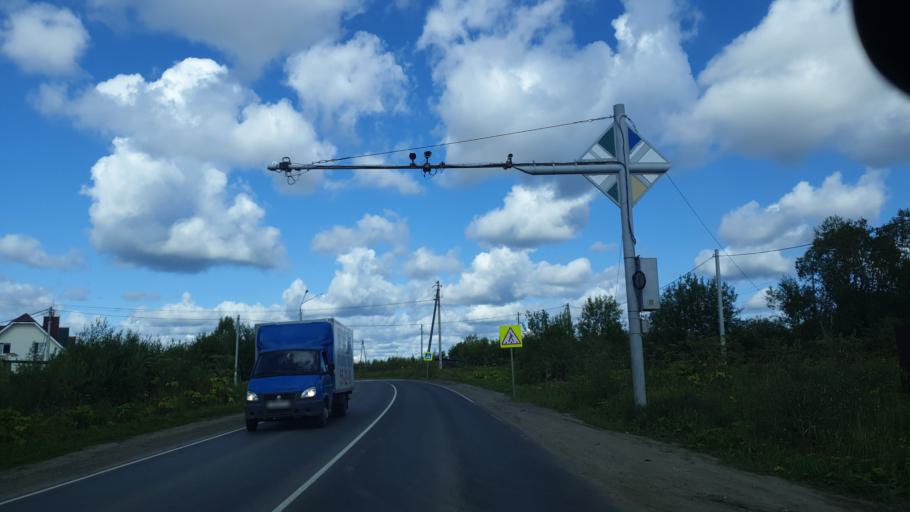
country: RU
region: Komi Republic
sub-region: Syktyvdinskiy Rayon
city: Syktyvkar
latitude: 61.6382
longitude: 50.8019
